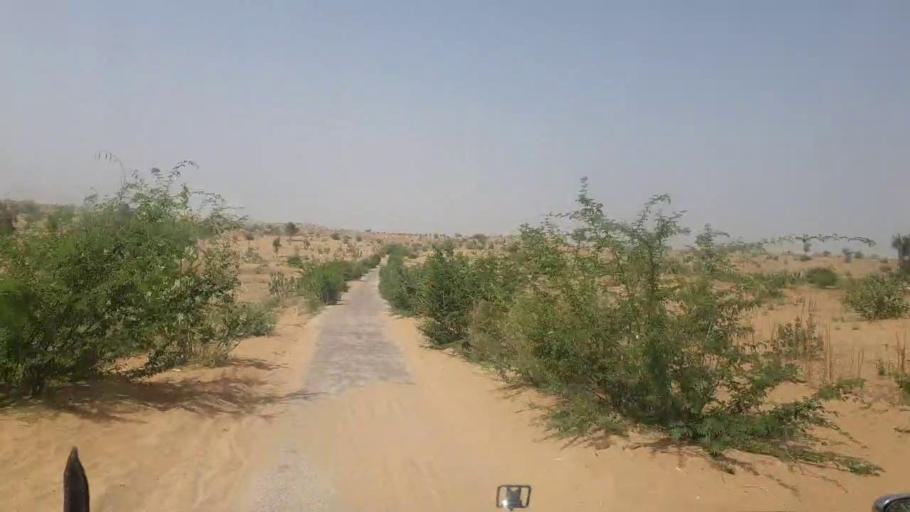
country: PK
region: Sindh
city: Islamkot
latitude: 25.1344
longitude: 70.2098
